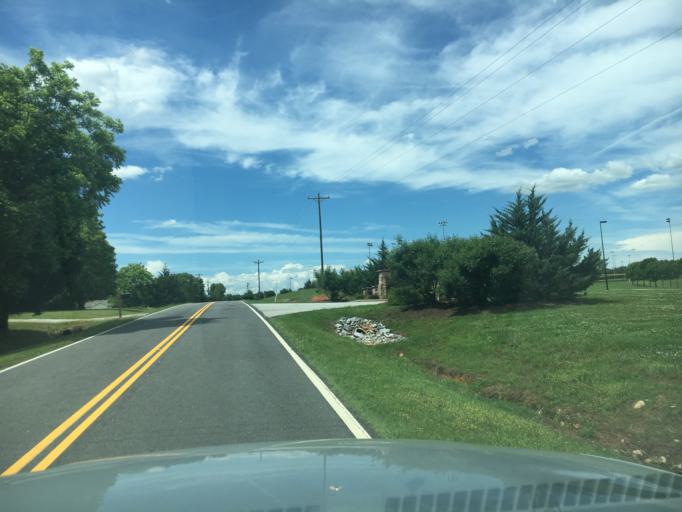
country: US
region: South Carolina
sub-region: Spartanburg County
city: Duncan
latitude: 34.8687
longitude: -82.1066
